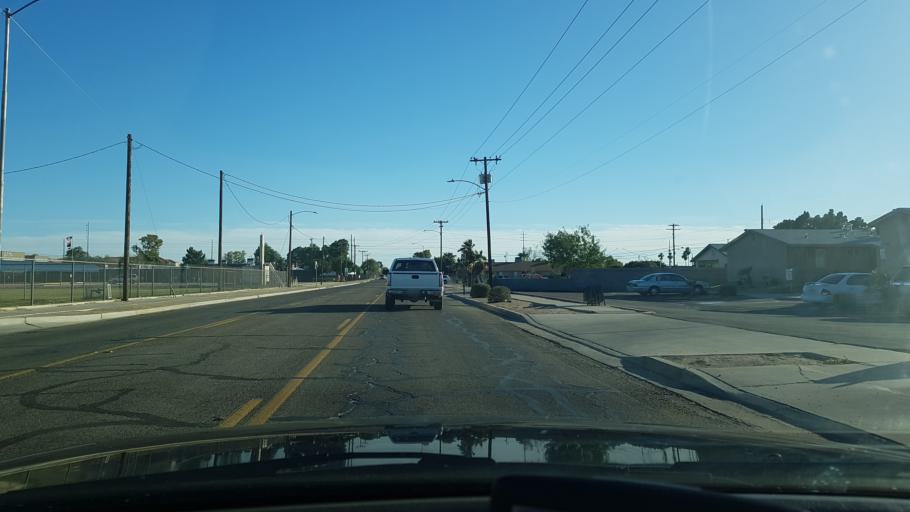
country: US
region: Arizona
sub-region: Yuma County
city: Yuma
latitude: 32.6870
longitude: -114.6160
